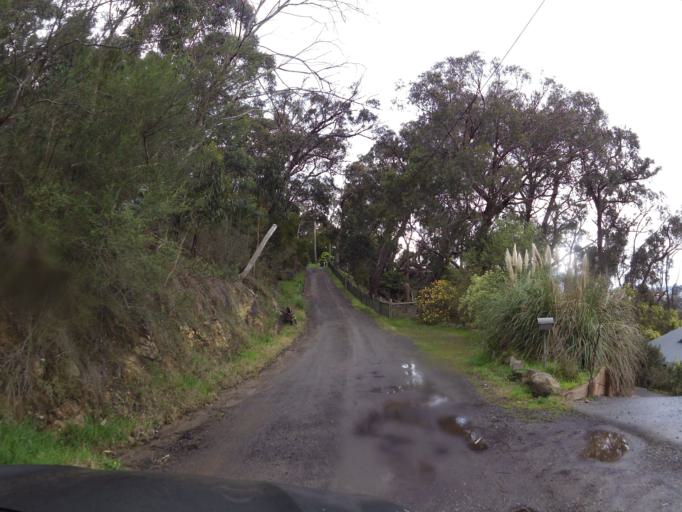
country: AU
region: Victoria
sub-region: Knox
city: Boronia
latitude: -37.8650
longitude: 145.3024
